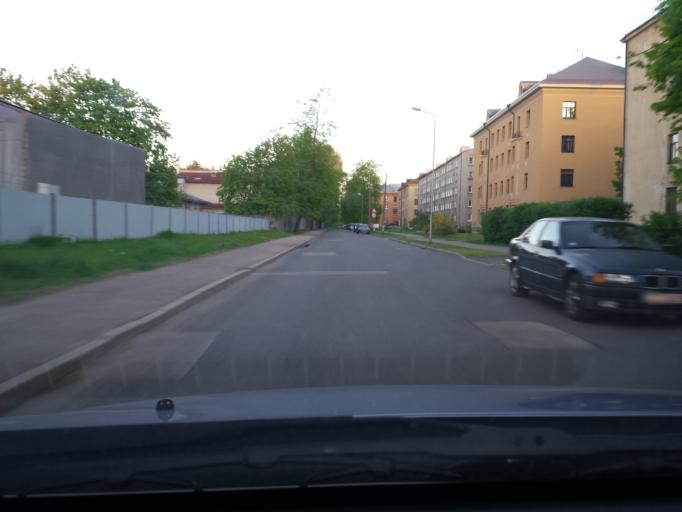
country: LV
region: Riga
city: Riga
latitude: 56.9902
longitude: 24.1342
